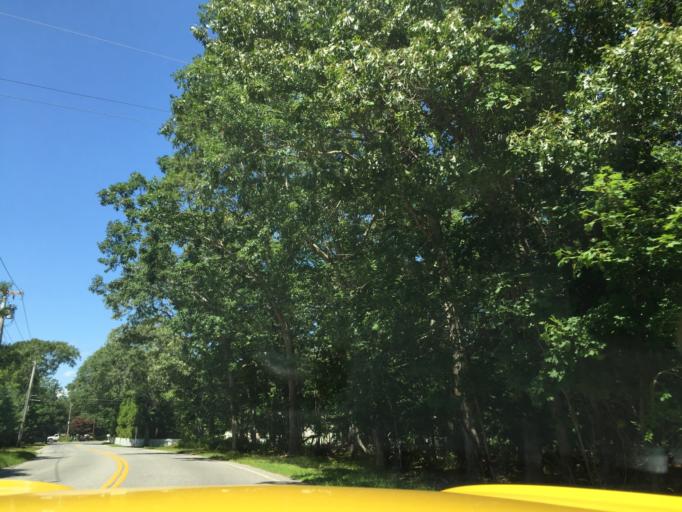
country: US
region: New York
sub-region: Suffolk County
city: Springs
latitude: 41.0017
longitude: -72.1330
